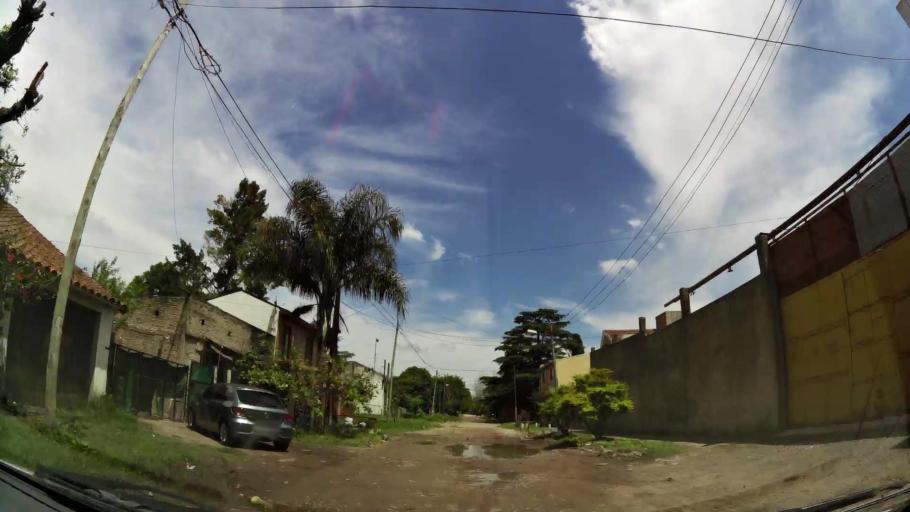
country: AR
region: Buenos Aires
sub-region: Partido de Quilmes
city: Quilmes
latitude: -34.7863
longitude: -58.2577
